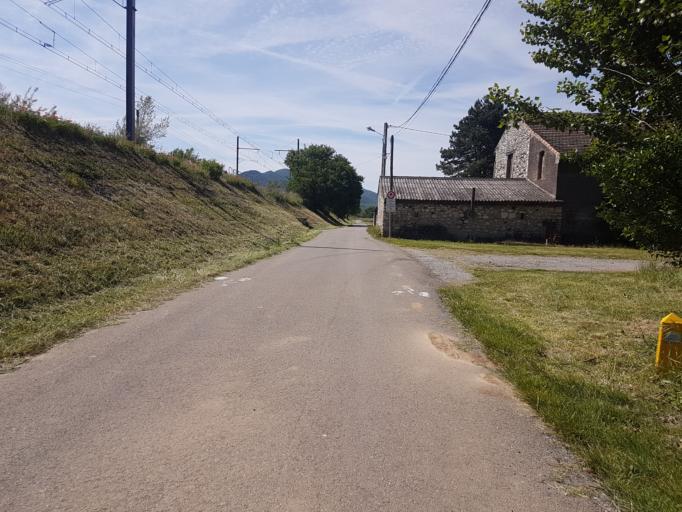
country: FR
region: Rhone-Alpes
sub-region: Departement de l'Ardeche
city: Le Pouzin
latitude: 44.7369
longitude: 4.7474
